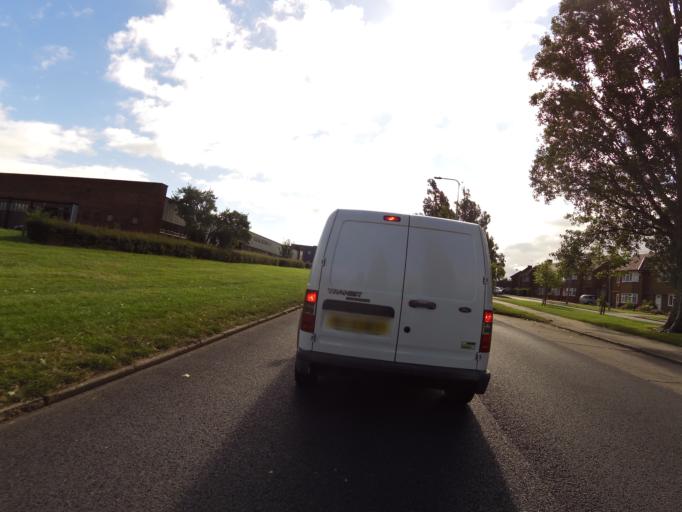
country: GB
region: England
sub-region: Suffolk
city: Bramford
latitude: 52.0804
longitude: 1.1198
